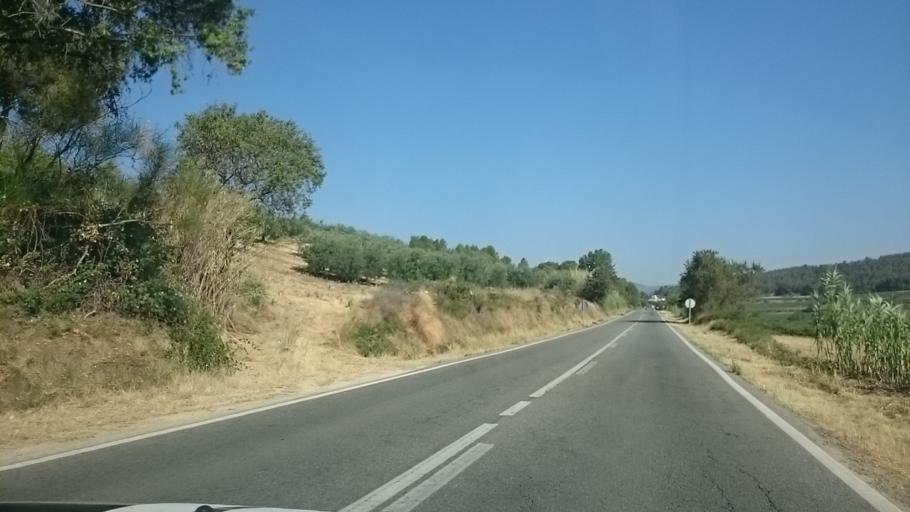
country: ES
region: Catalonia
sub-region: Provincia de Barcelona
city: Vilobi del Penedes
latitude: 41.3749
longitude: 1.6466
